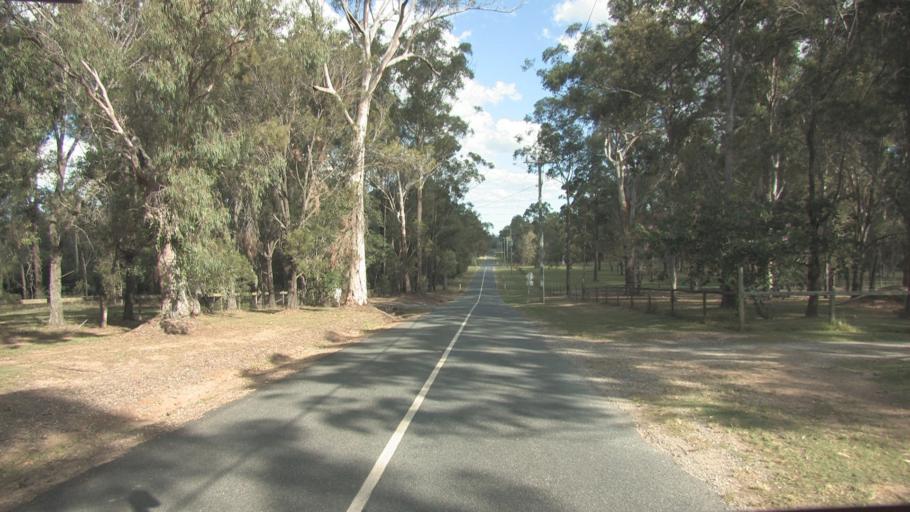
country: AU
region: Queensland
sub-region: Gold Coast
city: Yatala
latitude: -27.6592
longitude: 153.2417
